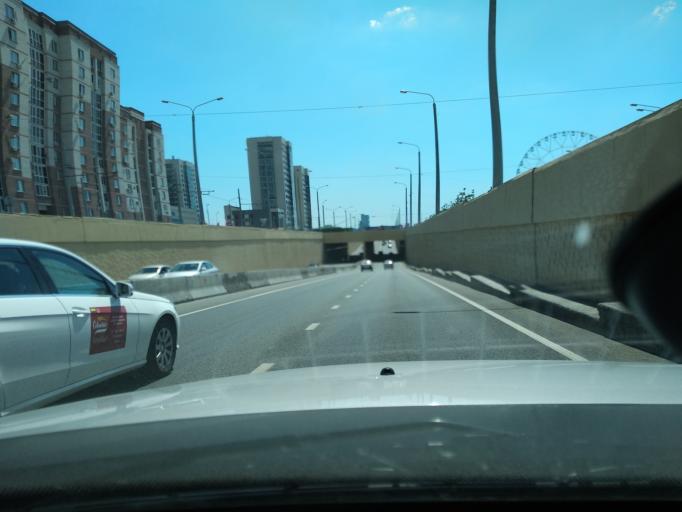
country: RU
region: Tatarstan
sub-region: Gorod Kazan'
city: Kazan
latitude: 55.8174
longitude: 49.1337
